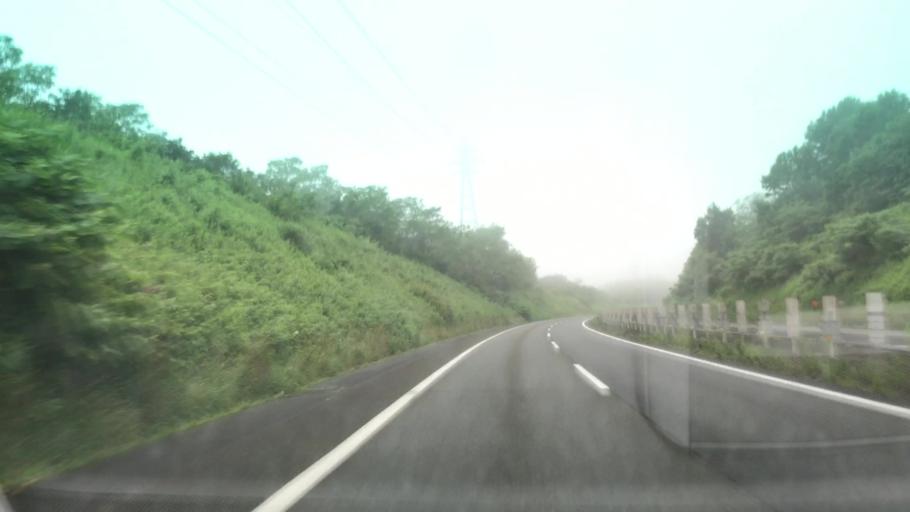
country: JP
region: Hokkaido
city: Tomakomai
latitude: 42.6659
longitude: 141.6111
